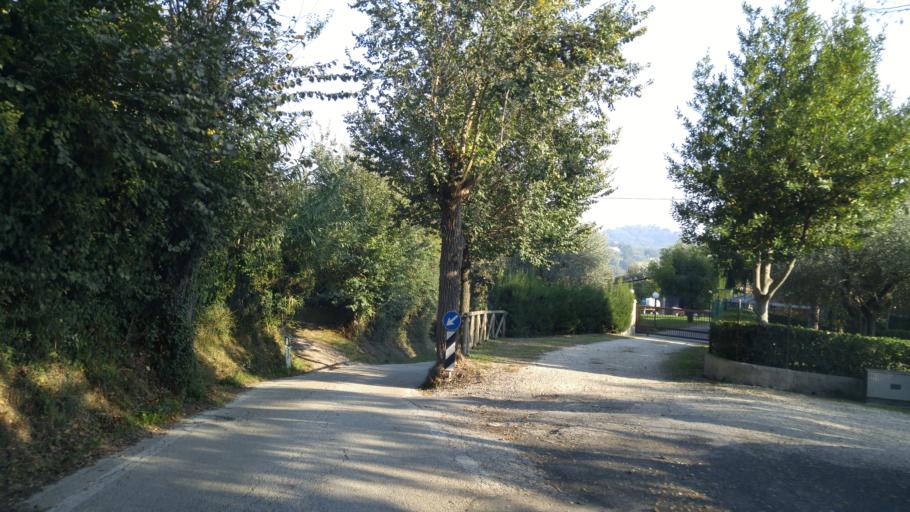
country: IT
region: The Marches
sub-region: Provincia di Pesaro e Urbino
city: Fenile
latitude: 43.8722
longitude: 12.9467
